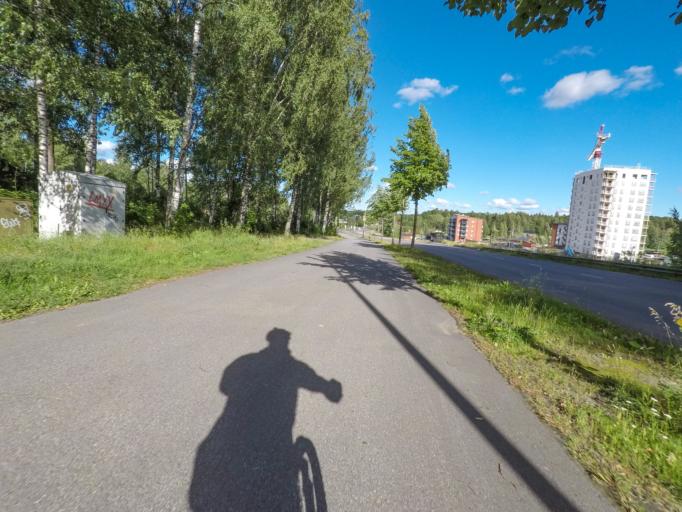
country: FI
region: South Karelia
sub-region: Lappeenranta
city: Lappeenranta
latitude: 61.0650
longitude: 28.1625
